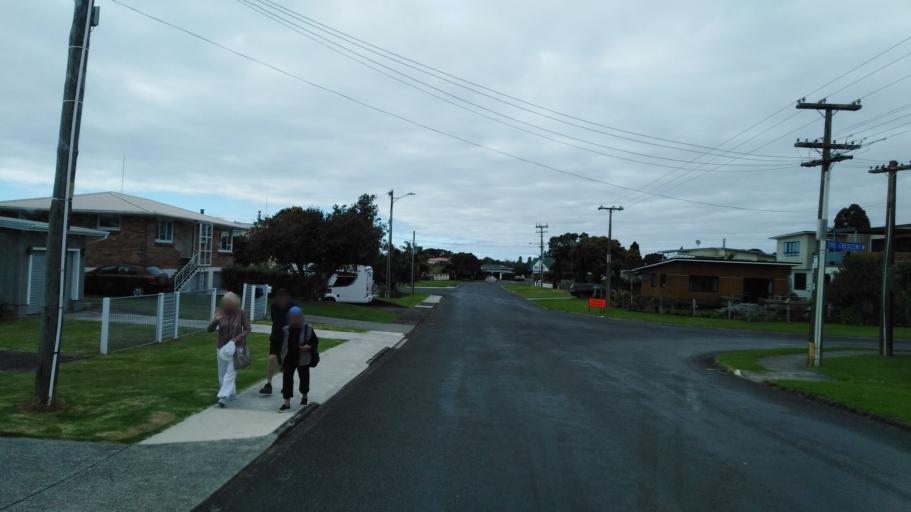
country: NZ
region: Bay of Plenty
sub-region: Western Bay of Plenty District
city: Waihi Beach
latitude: -37.4129
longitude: 175.9423
